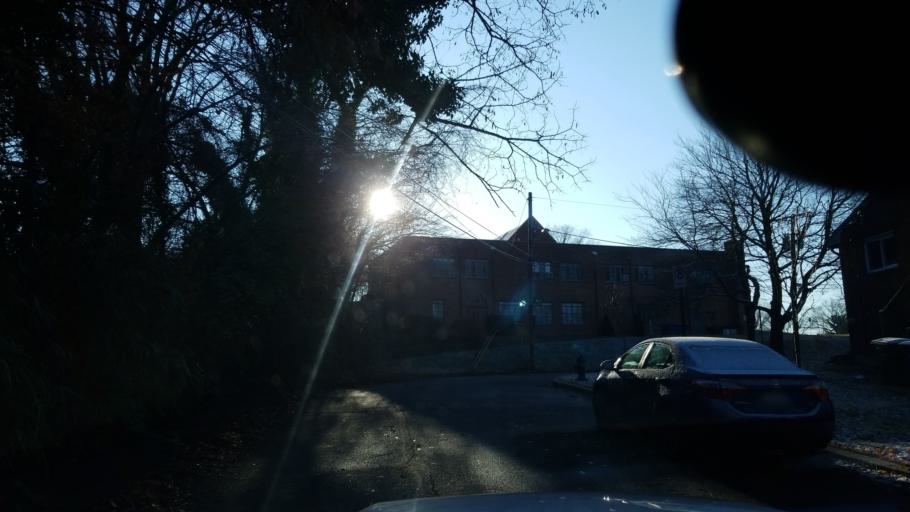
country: US
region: Maryland
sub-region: Montgomery County
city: Friendship Village
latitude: 38.9409
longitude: -77.0852
